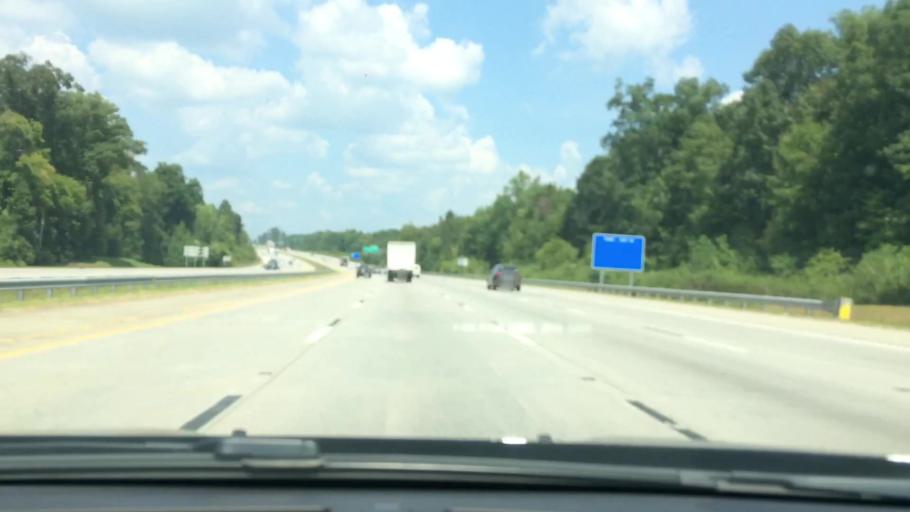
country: US
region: North Carolina
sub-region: Rowan County
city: East Spencer
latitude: 35.6834
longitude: -80.4069
